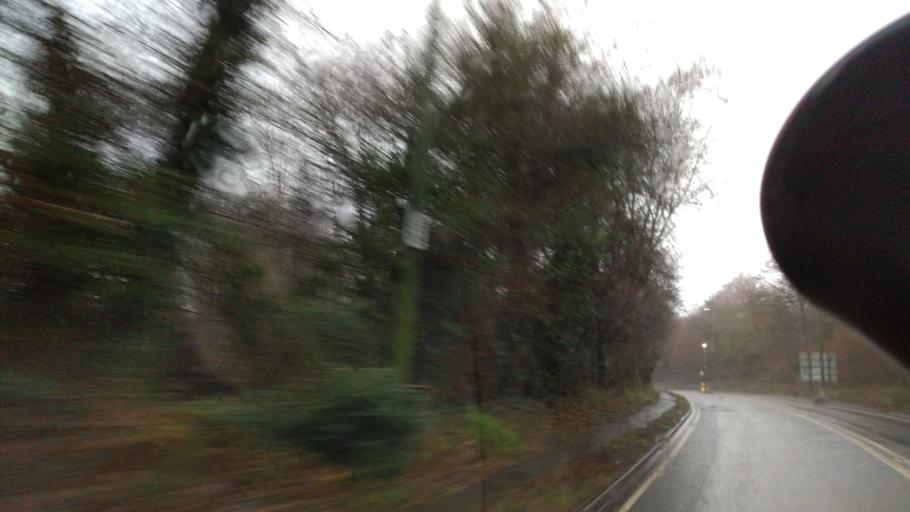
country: GB
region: England
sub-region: West Sussex
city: Arundel
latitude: 50.8539
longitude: -0.5657
